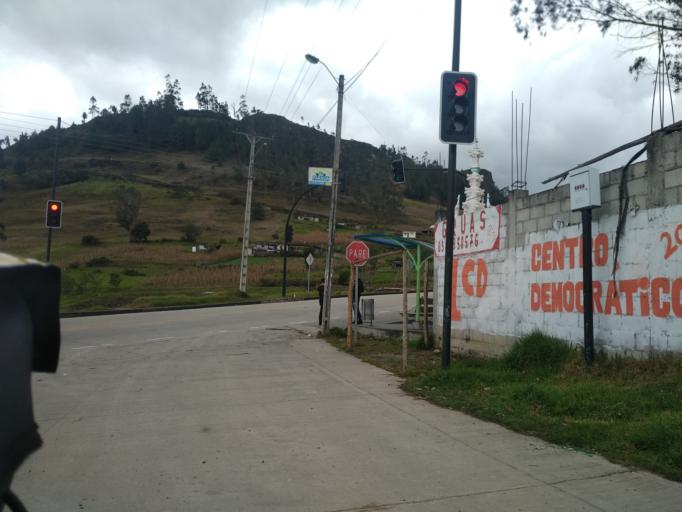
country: EC
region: Loja
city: Loja
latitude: -3.6036
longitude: -79.2108
